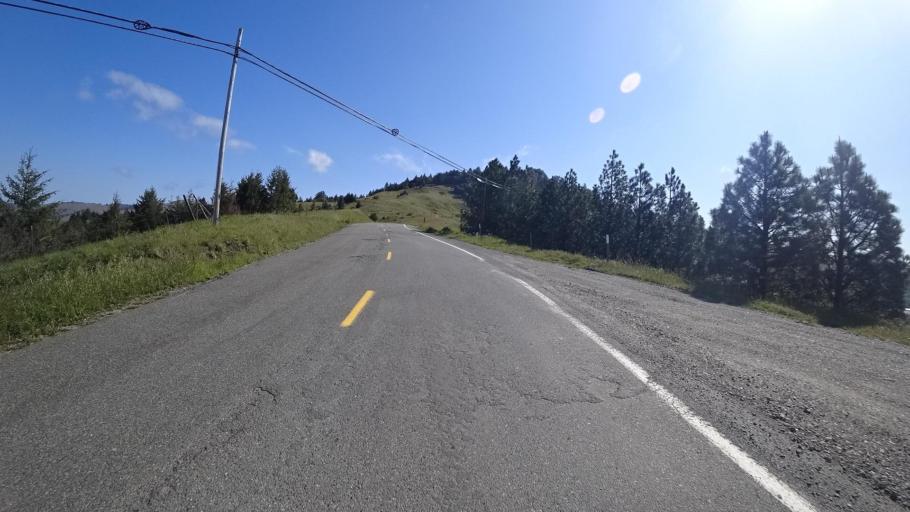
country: US
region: California
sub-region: Humboldt County
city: Redway
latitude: 40.1114
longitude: -123.7412
